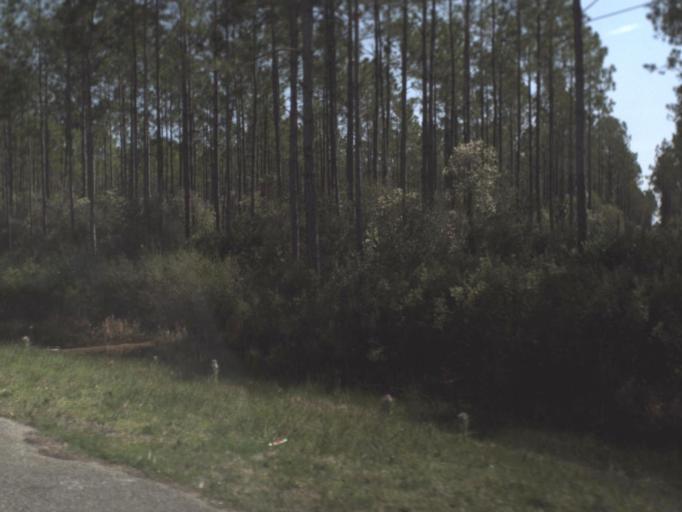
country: US
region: Florida
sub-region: Franklin County
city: Apalachicola
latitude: 29.7300
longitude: -85.1381
